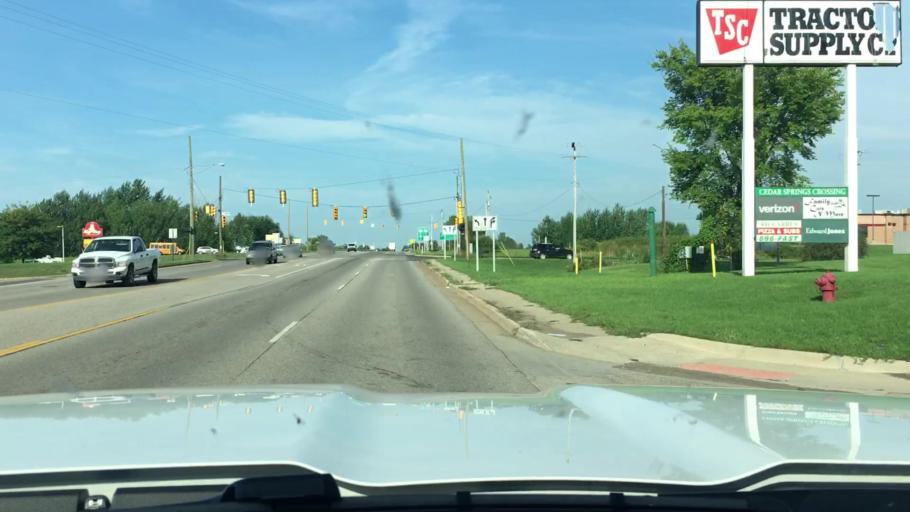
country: US
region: Michigan
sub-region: Kent County
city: Cedar Springs
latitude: 43.2199
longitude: -85.5700
